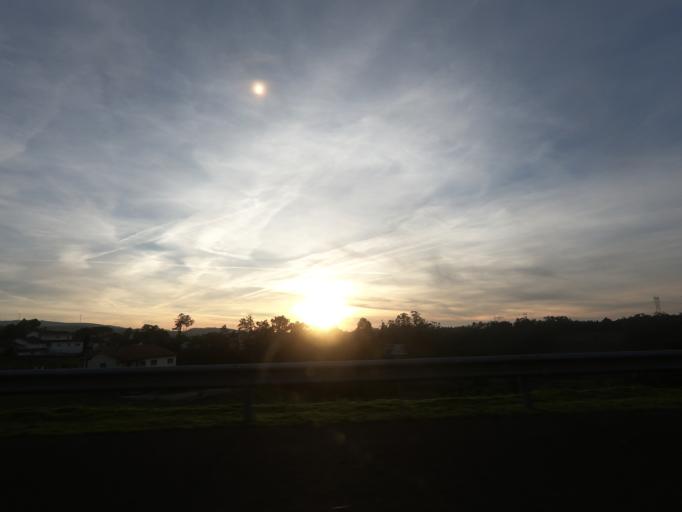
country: PT
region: Leiria
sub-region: Leiria
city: Caranguejeira
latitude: 39.7349
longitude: -8.7295
